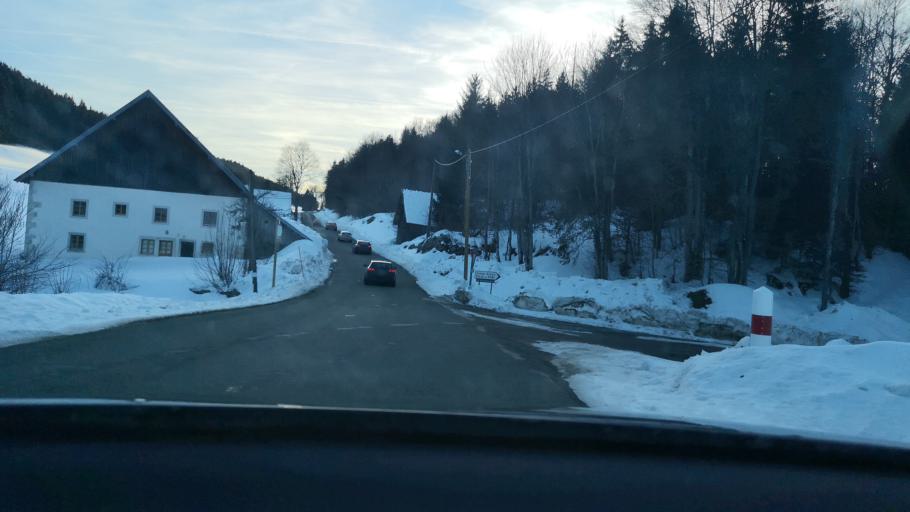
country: FR
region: Franche-Comte
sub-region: Departement du Doubs
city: Gilley
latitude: 46.9814
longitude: 6.4995
